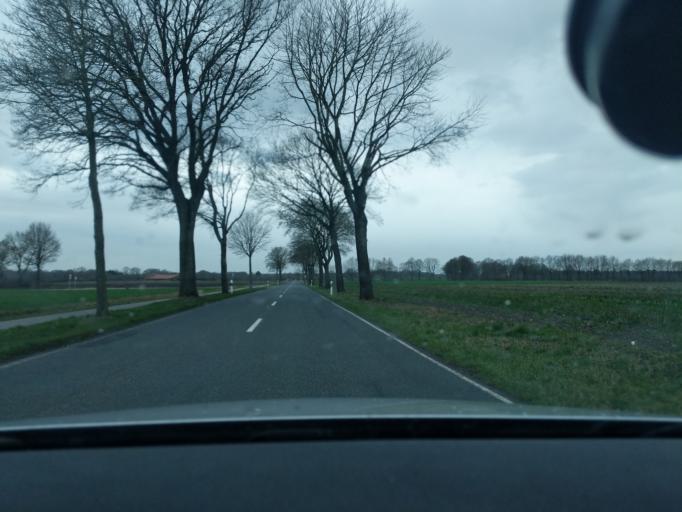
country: DE
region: Lower Saxony
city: Deinstedt
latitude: 53.4821
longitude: 9.2571
